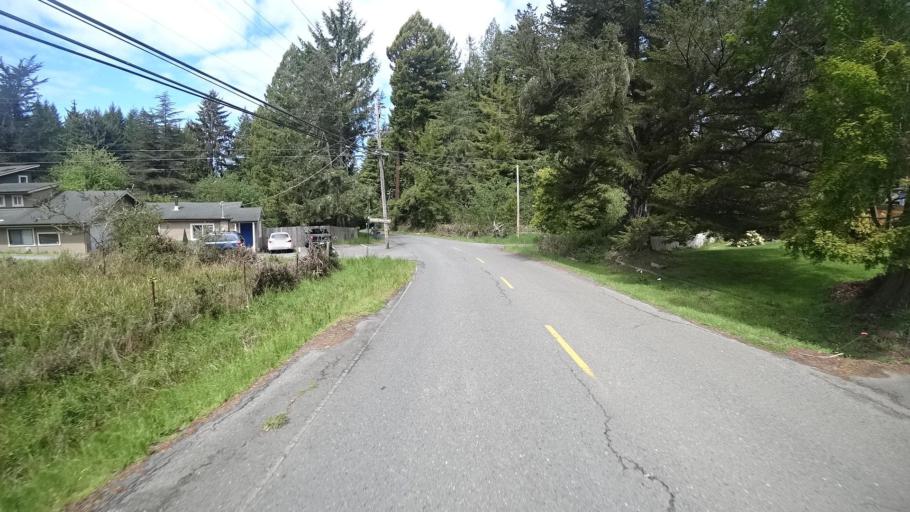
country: US
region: California
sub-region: Humboldt County
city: Bayside
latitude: 40.8653
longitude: -124.0447
